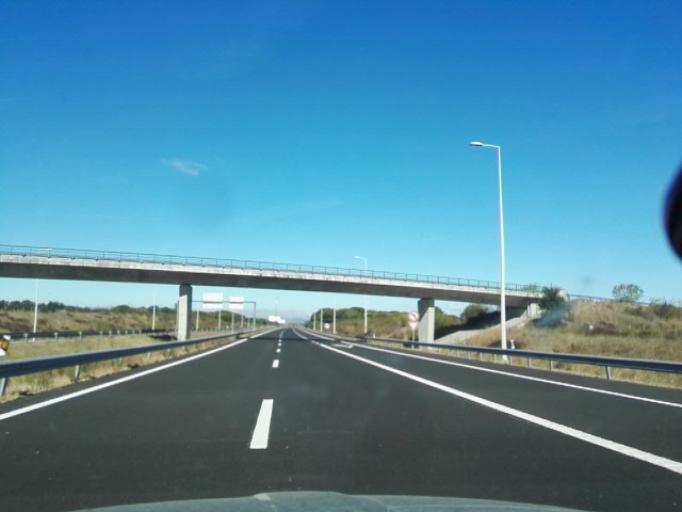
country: PT
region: Santarem
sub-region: Benavente
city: Benavente
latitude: 38.9093
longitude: -8.7868
